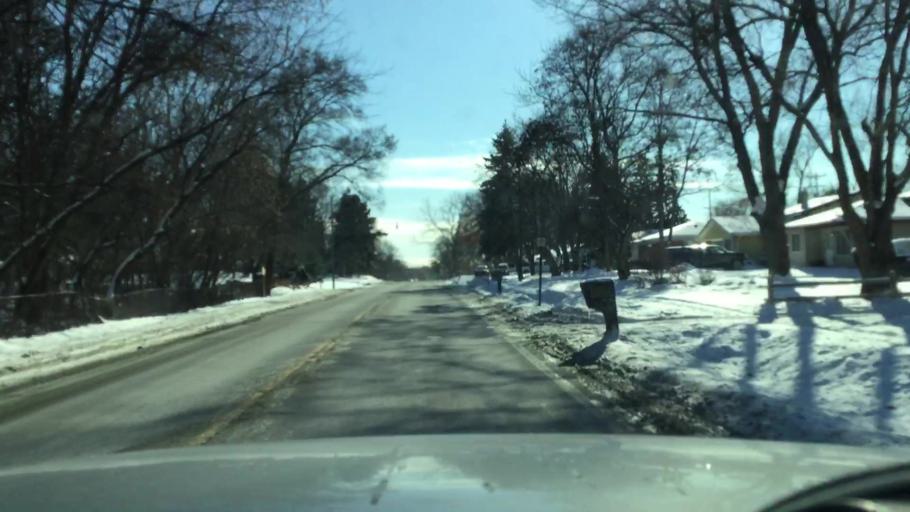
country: US
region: Michigan
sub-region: Oakland County
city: Keego Harbor
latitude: 42.6295
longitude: -83.3550
